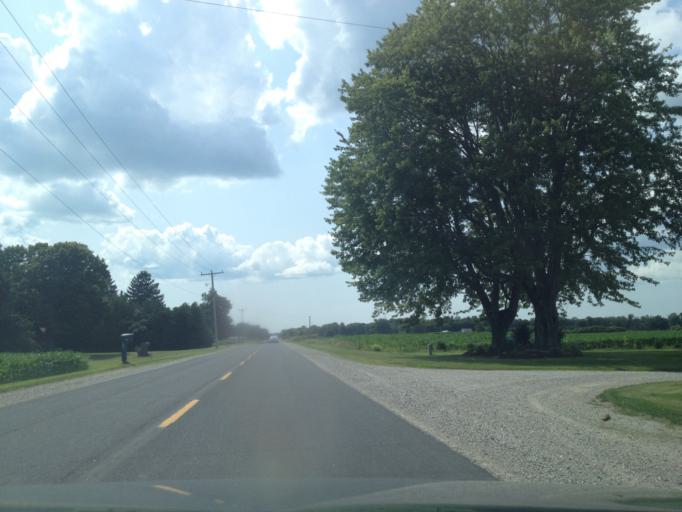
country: CA
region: Ontario
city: Aylmer
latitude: 42.6750
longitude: -80.9406
